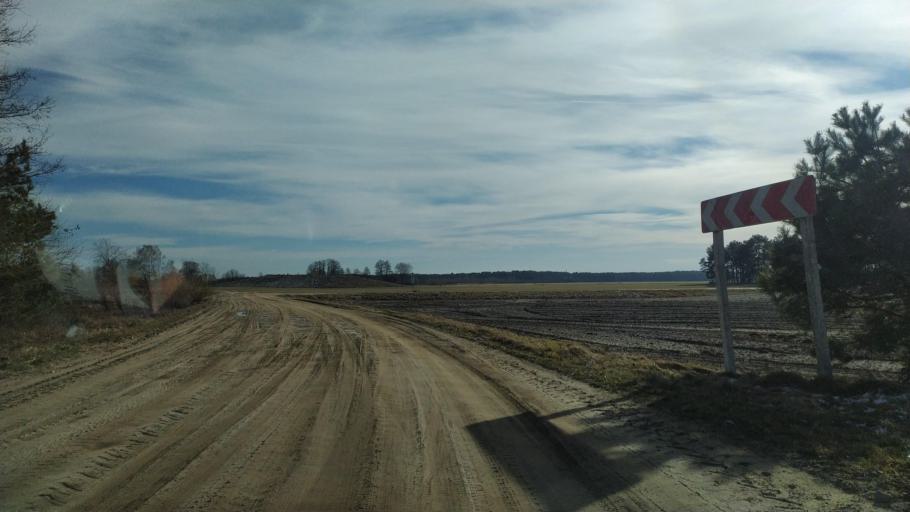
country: BY
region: Brest
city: Pruzhany
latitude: 52.5757
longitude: 24.3019
